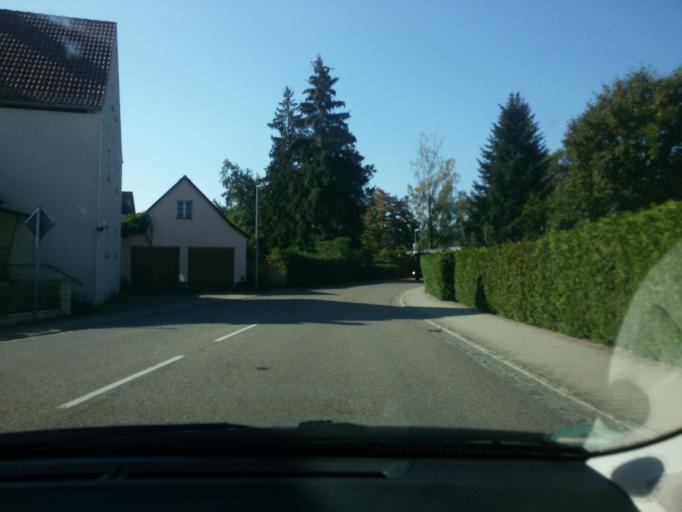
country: DE
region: Bavaria
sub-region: Regierungsbezirk Mittelfranken
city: Wassertrudingen
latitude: 49.0406
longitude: 10.6045
